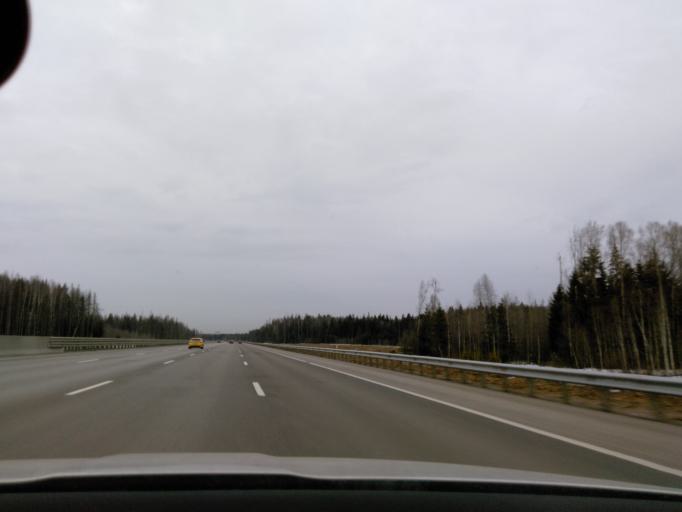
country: RU
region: Moskovskaya
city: Rzhavki
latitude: 55.9988
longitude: 37.2961
